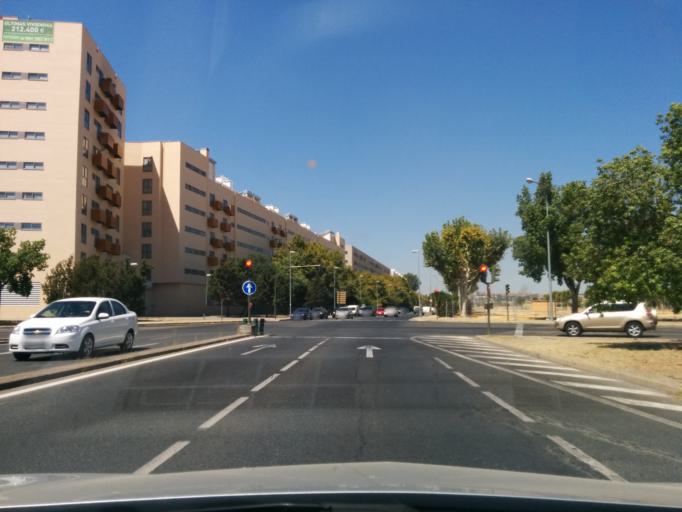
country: ES
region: Andalusia
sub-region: Provincia de Sevilla
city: Sevilla
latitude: 37.3679
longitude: -5.9975
